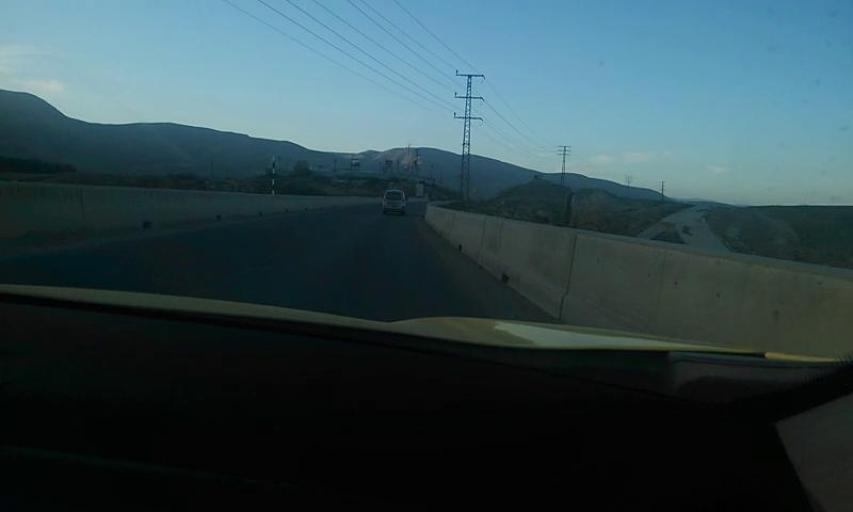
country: PS
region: West Bank
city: An Nuway`imah
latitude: 31.9094
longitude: 35.4226
